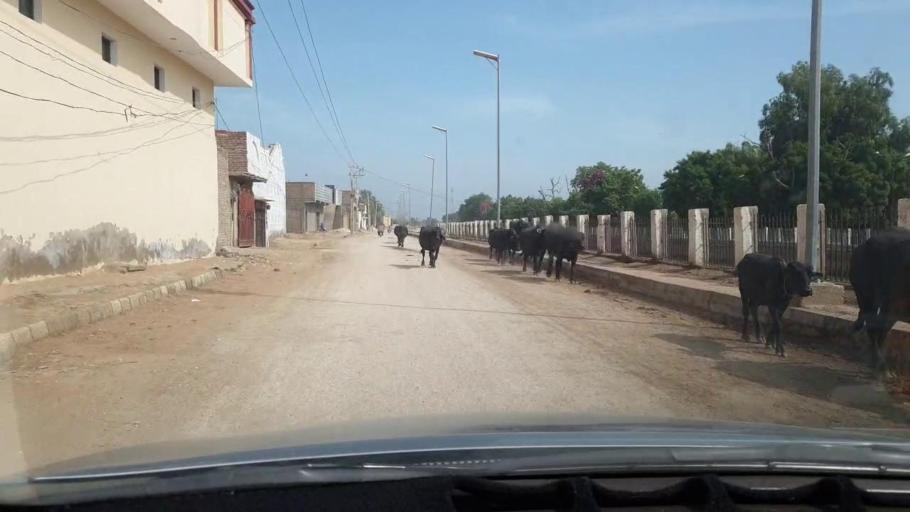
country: PK
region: Sindh
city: Khairpur
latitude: 27.5166
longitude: 68.7585
